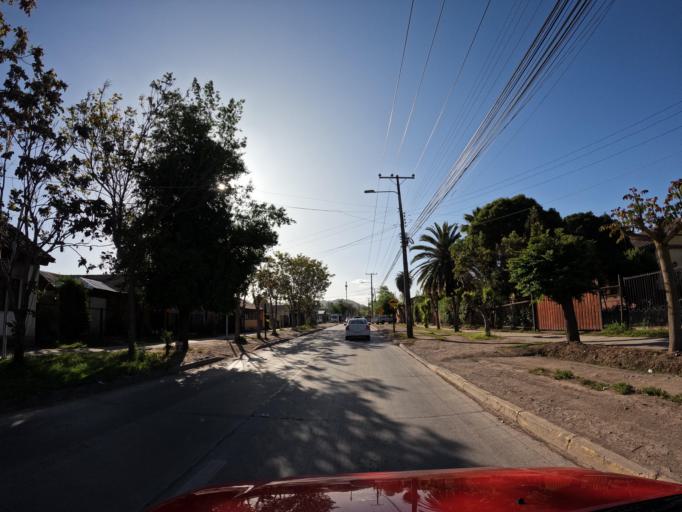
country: CL
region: O'Higgins
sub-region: Provincia de Colchagua
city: Santa Cruz
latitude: -34.7254
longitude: -71.2780
